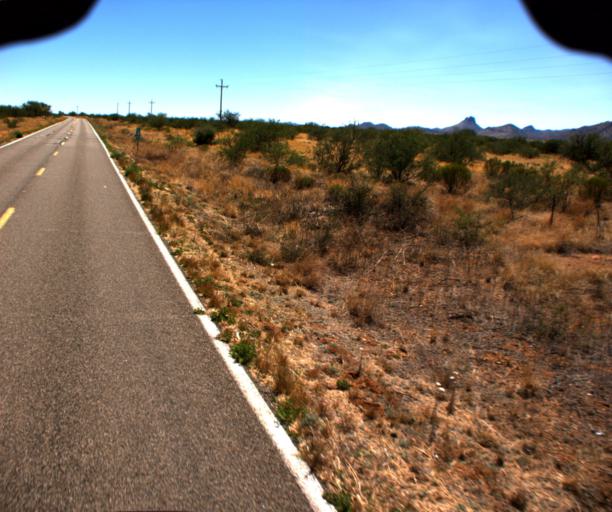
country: US
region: Arizona
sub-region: Pima County
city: Three Points
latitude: 31.7573
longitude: -111.4773
